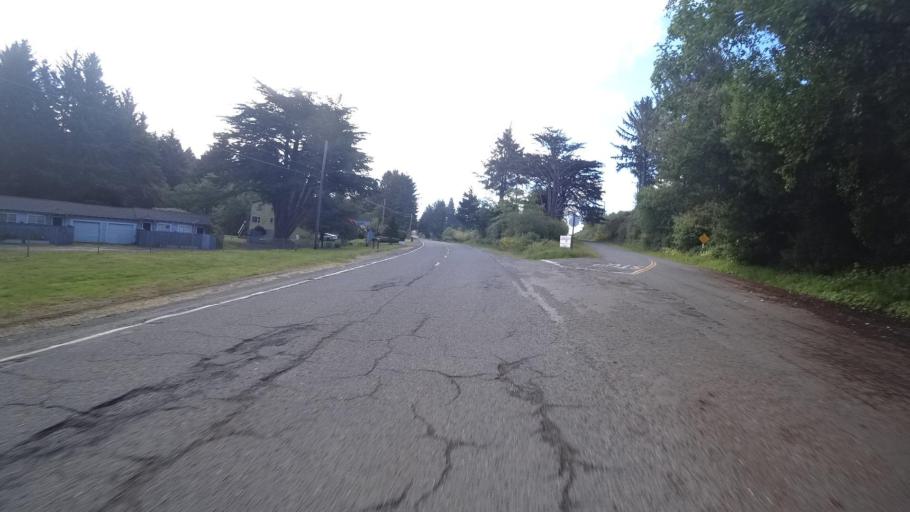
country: US
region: California
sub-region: Humboldt County
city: McKinleyville
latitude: 40.9886
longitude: -124.1097
